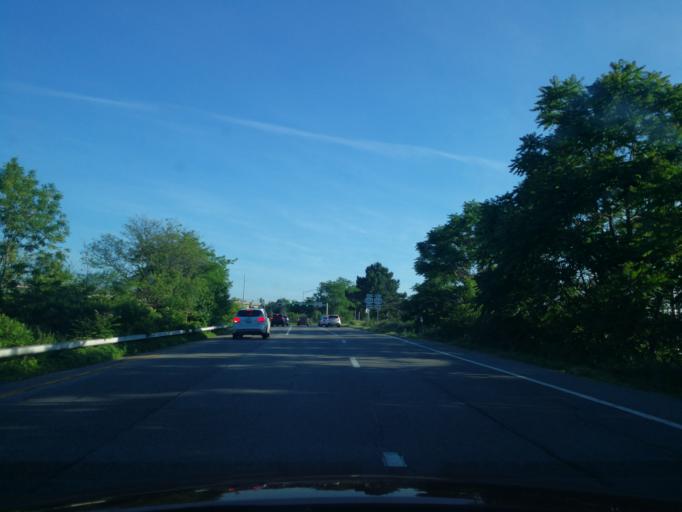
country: US
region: New York
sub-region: Monroe County
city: Greece
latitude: 43.2078
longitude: -77.6763
